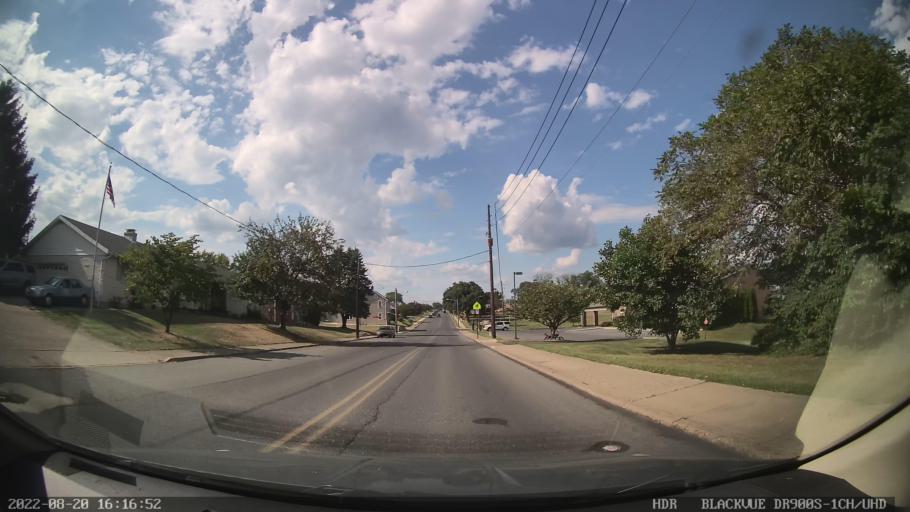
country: US
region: Pennsylvania
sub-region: Northampton County
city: Northampton
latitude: 40.6842
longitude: -75.4912
